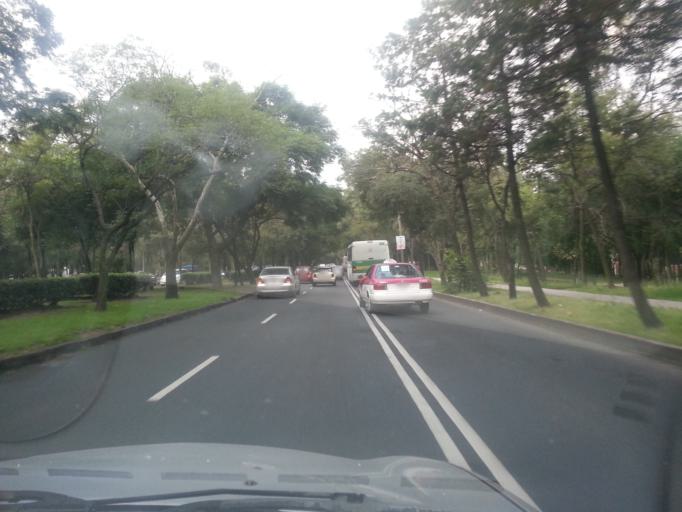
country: MX
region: Mexico City
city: Polanco
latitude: 19.4110
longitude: -99.2217
